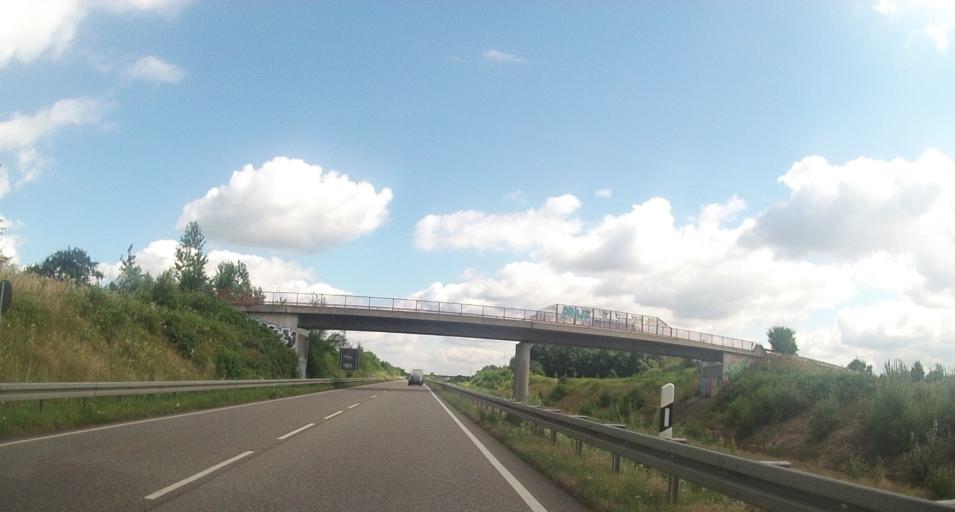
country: DE
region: Baden-Wuerttemberg
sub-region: Karlsruhe Region
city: Durmersheim
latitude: 48.9268
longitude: 8.2760
